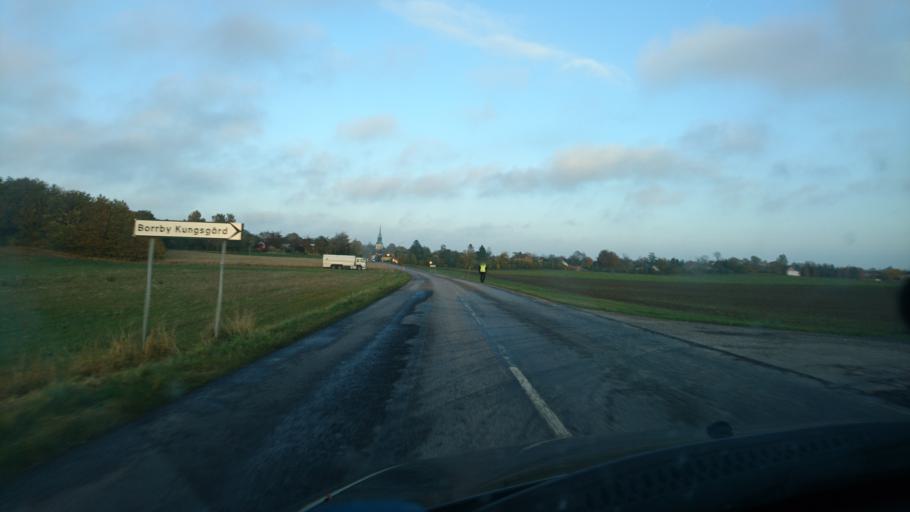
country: SE
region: Skane
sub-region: Simrishamns Kommun
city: Simrishamn
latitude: 55.4551
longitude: 14.1663
